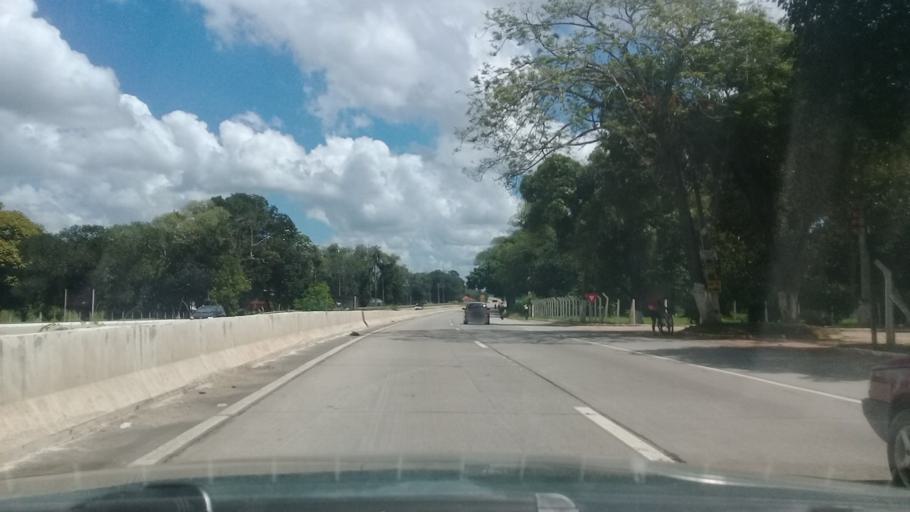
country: BR
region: Pernambuco
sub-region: Carpina
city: Carpina
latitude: -7.9238
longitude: -35.1548
